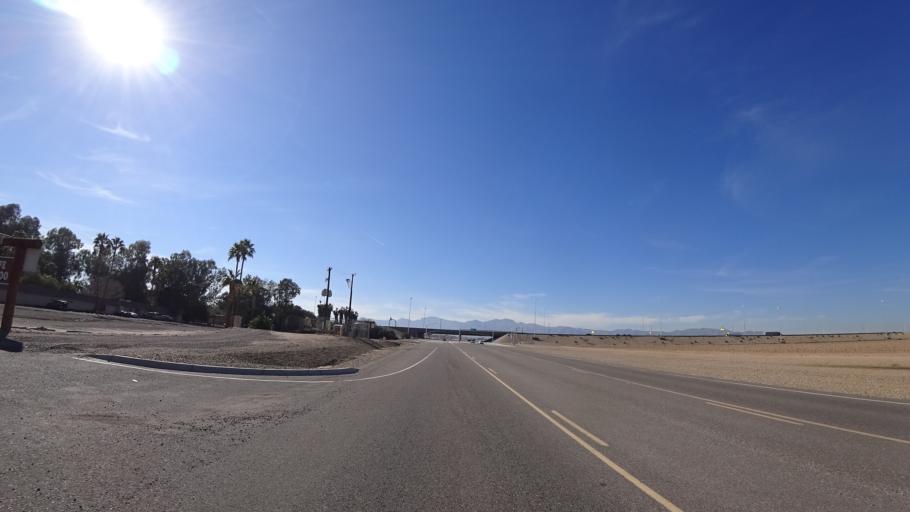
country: US
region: Arizona
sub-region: Maricopa County
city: Citrus Park
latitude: 33.5516
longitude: -112.4148
